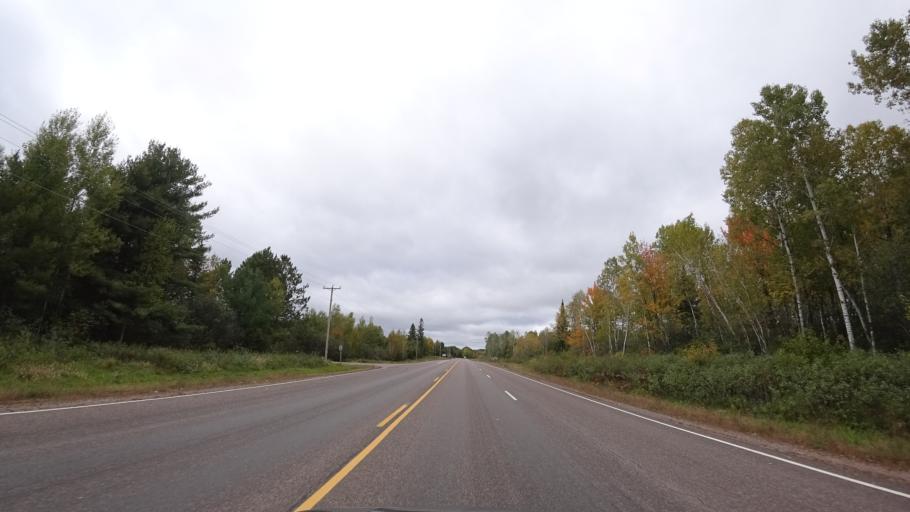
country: US
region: Wisconsin
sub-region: Rusk County
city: Ladysmith
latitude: 45.4431
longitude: -91.1111
